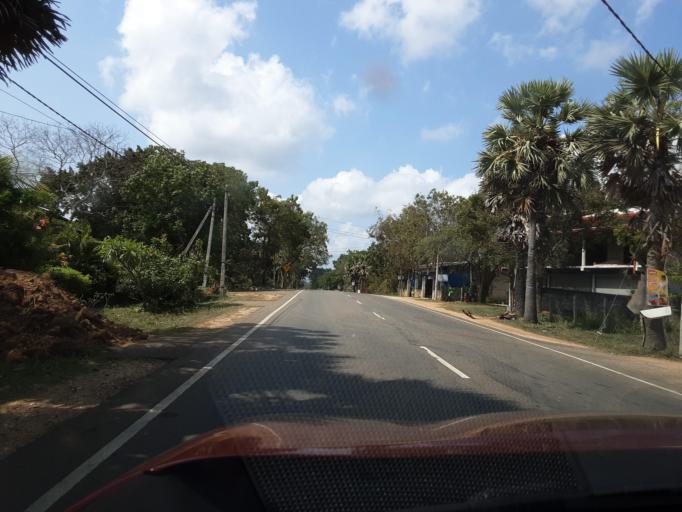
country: LK
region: Southern
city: Tangalla
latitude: 6.2704
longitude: 81.2273
